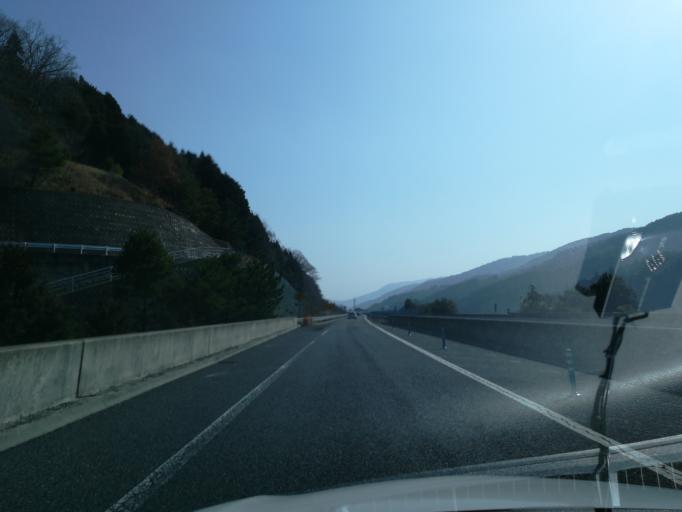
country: JP
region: Tokushima
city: Ikedacho
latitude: 34.0065
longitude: 133.7132
